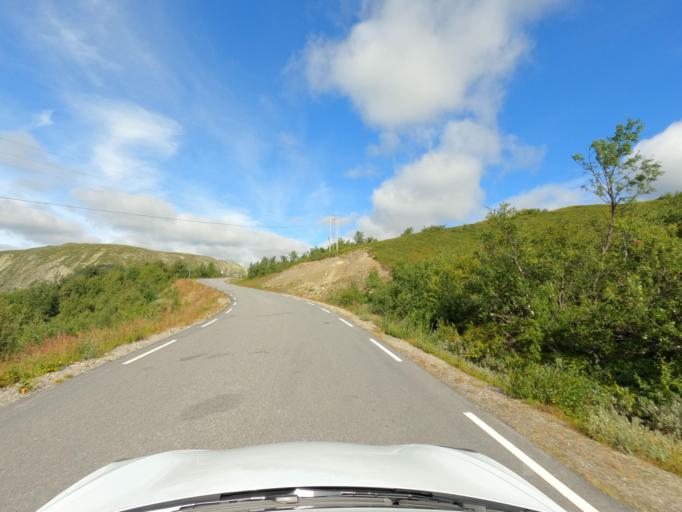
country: NO
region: Telemark
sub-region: Tinn
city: Rjukan
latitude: 60.1497
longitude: 8.6263
